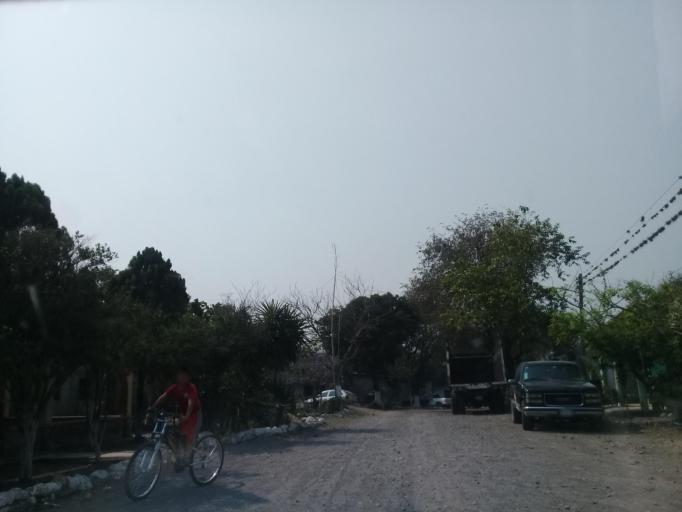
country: MX
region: Oaxaca
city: Acatlan de Perez Figueroa
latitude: 18.6047
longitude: -96.5773
